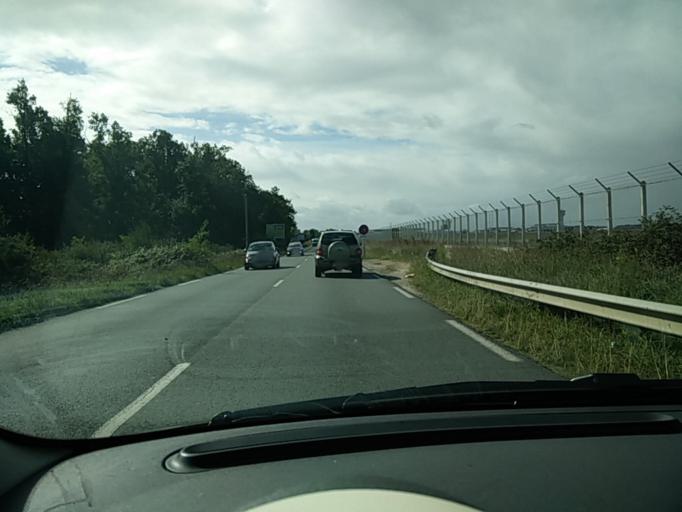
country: FR
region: Aquitaine
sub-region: Departement de la Gironde
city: Le Haillan
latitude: 44.8425
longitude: -0.6931
